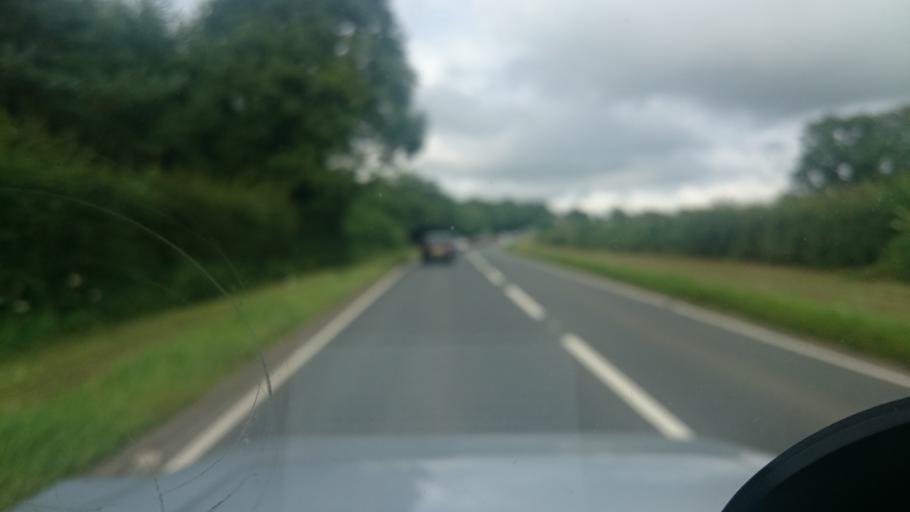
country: GB
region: Wales
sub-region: Pembrokeshire
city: Narberth
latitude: 51.8102
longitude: -4.7589
